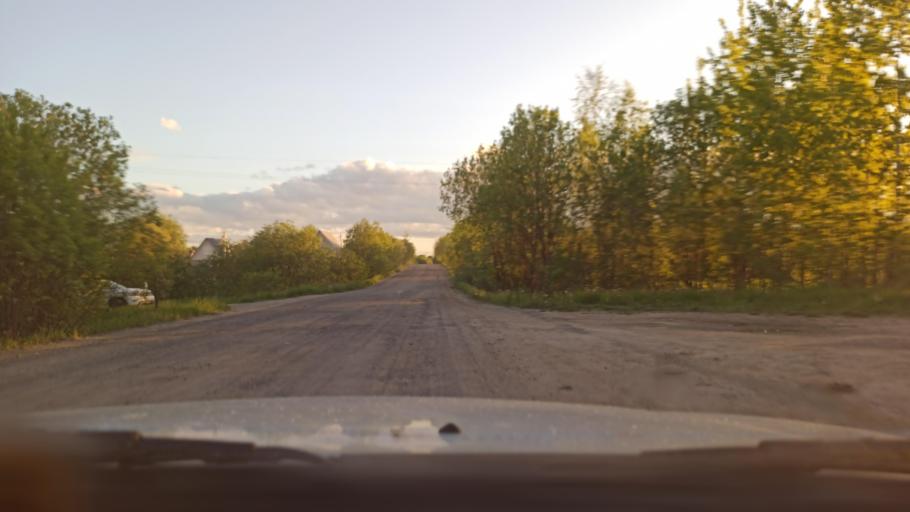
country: RU
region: Vologda
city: Molochnoye
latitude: 59.3688
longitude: 39.6786
